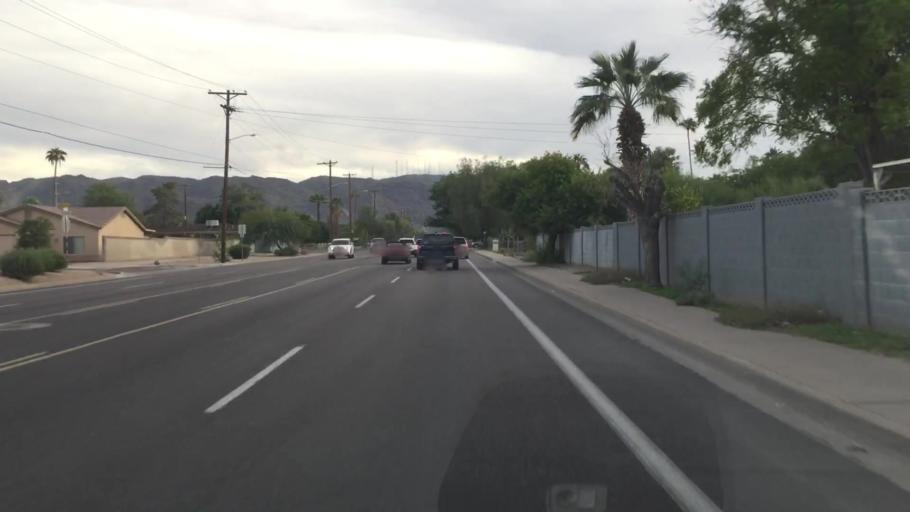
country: US
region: Arizona
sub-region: Maricopa County
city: Phoenix
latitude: 33.3837
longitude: -112.0647
